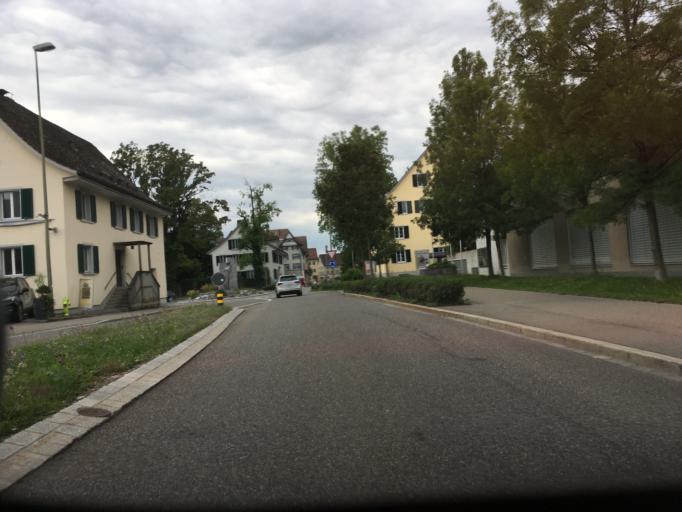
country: CH
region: Zurich
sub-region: Bezirk Pfaeffikon
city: Pfaeffikon / Pfaeffikon (Dorfkern)
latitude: 47.3654
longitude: 8.7859
